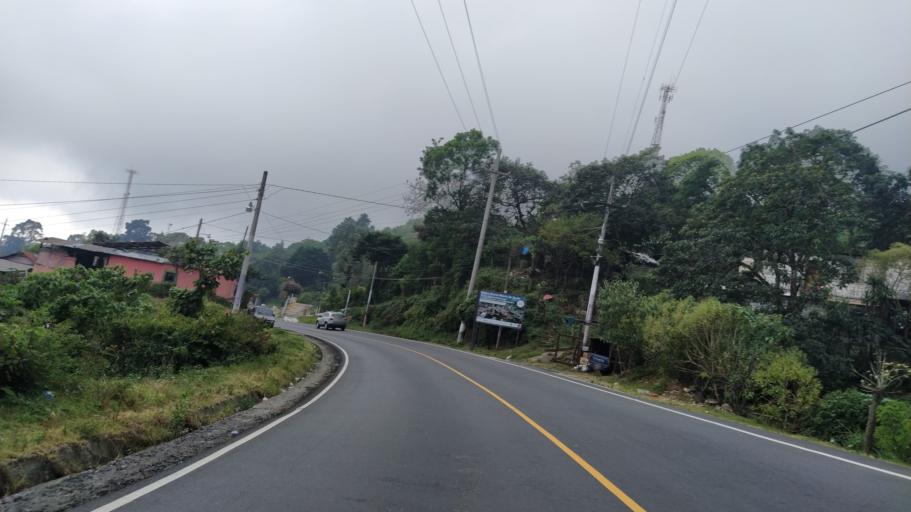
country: GT
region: Quetzaltenango
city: Zunil
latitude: 14.7259
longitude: -91.5272
